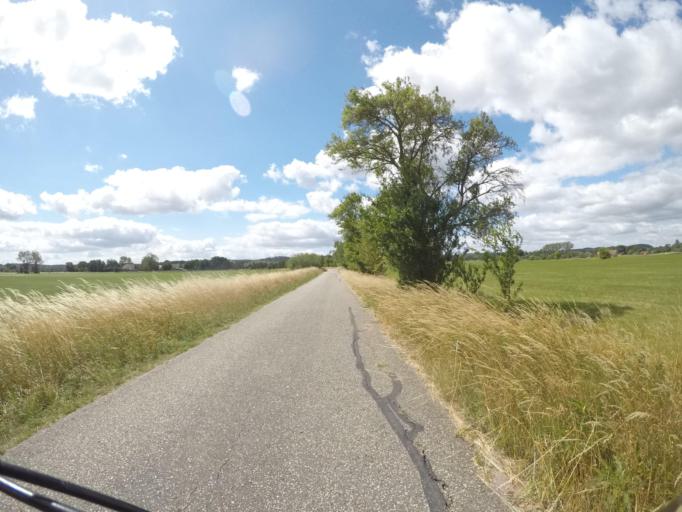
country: DE
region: Lower Saxony
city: Hitzacker
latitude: 53.1920
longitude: 11.0143
